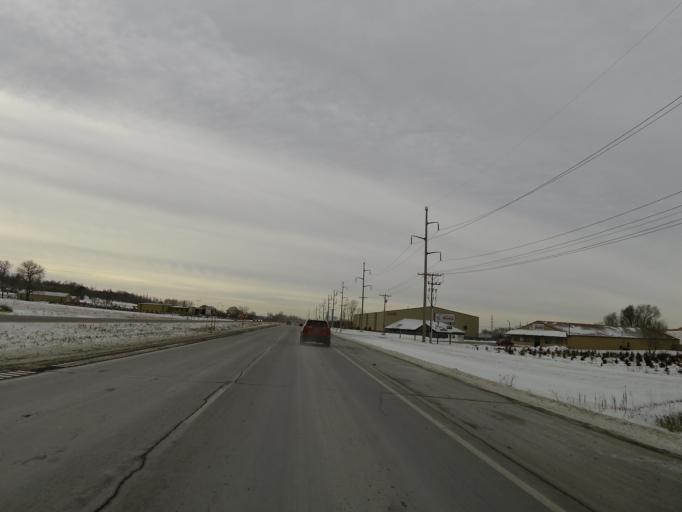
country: US
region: Minnesota
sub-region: Carver County
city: Chaska
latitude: 44.7612
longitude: -93.5823
